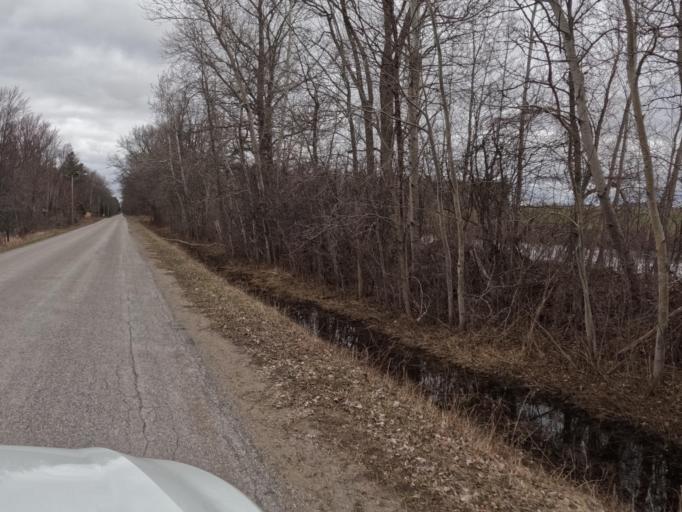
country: CA
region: Ontario
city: Norfolk County
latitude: 42.9741
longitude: -80.4015
